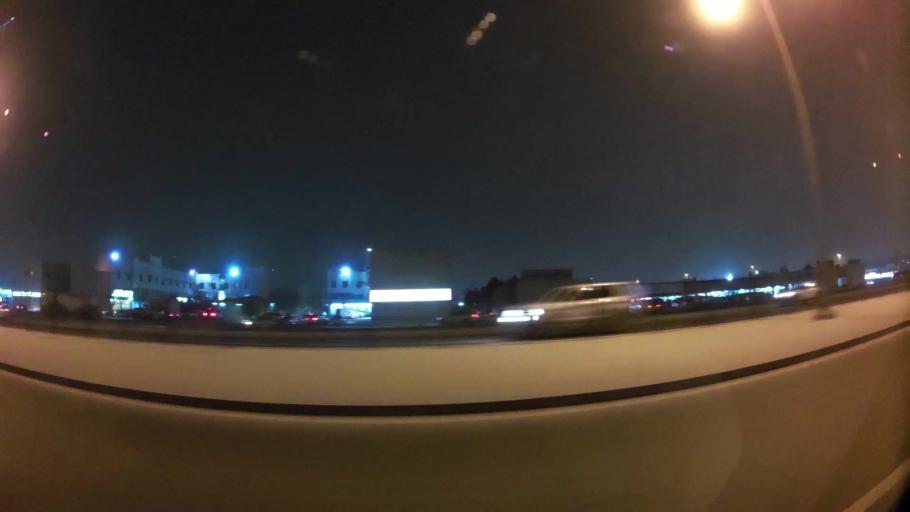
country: QA
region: Baladiyat ad Dawhah
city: Doha
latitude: 25.2466
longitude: 51.4736
